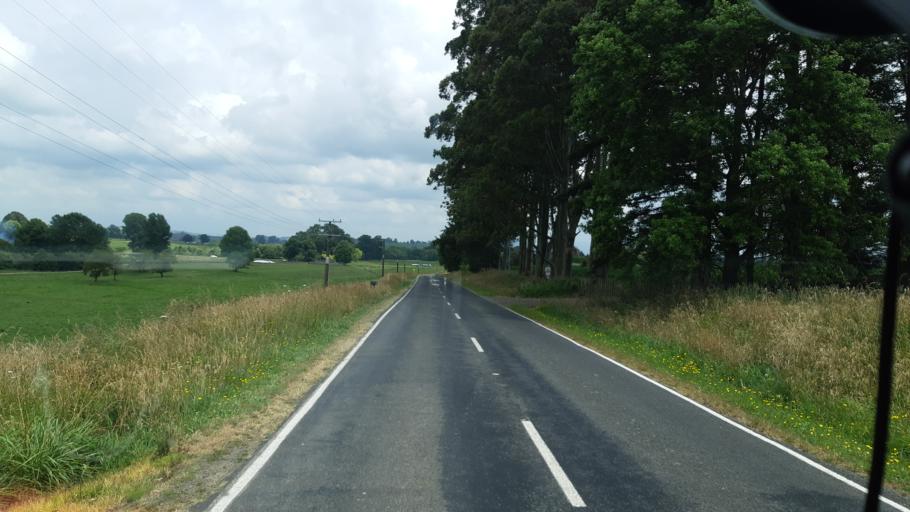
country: NZ
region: Waikato
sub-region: Waipa District
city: Cambridge
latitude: -38.1029
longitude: 175.4478
